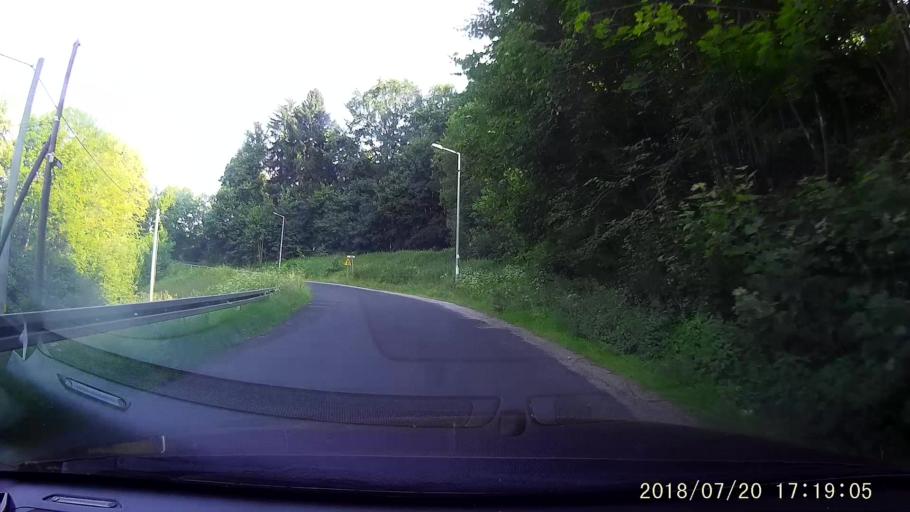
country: PL
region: Lower Silesian Voivodeship
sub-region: Powiat lubanski
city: Lesna
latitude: 50.9922
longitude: 15.2893
